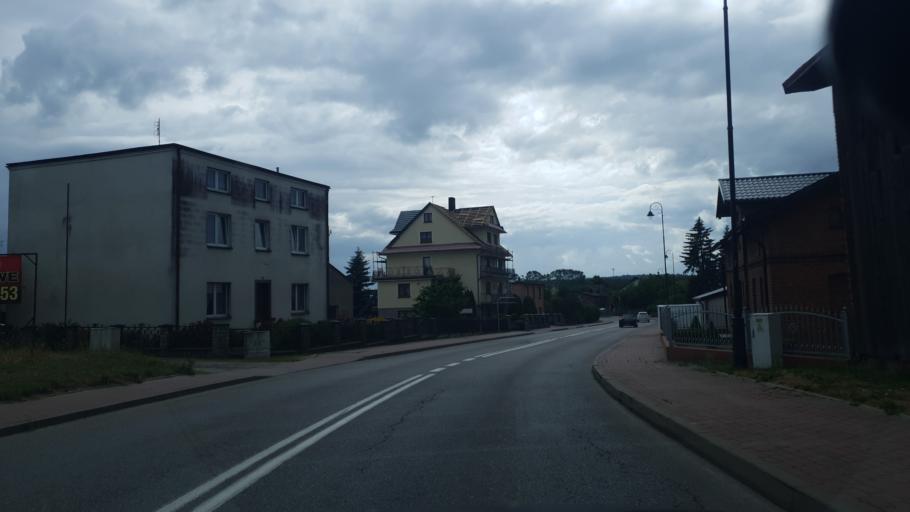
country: PL
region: Pomeranian Voivodeship
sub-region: Powiat kartuski
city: Przodkowo
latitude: 54.3763
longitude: 18.2866
